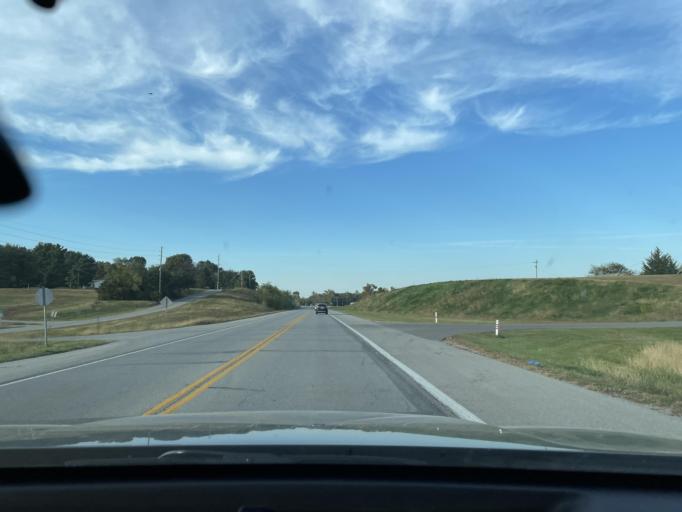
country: US
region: Missouri
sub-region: Andrew County
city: Country Club Village
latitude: 39.7776
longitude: -94.7675
